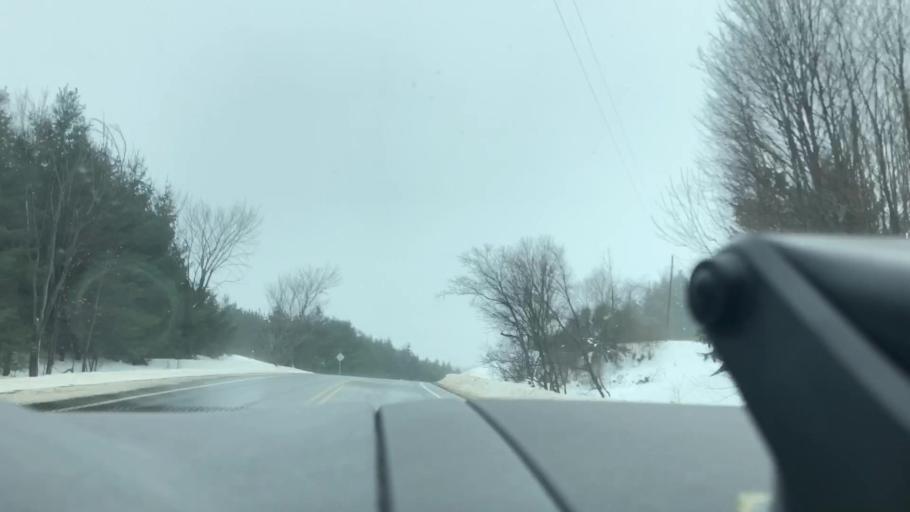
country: US
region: Michigan
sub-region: Charlevoix County
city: East Jordan
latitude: 45.1575
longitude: -85.1598
